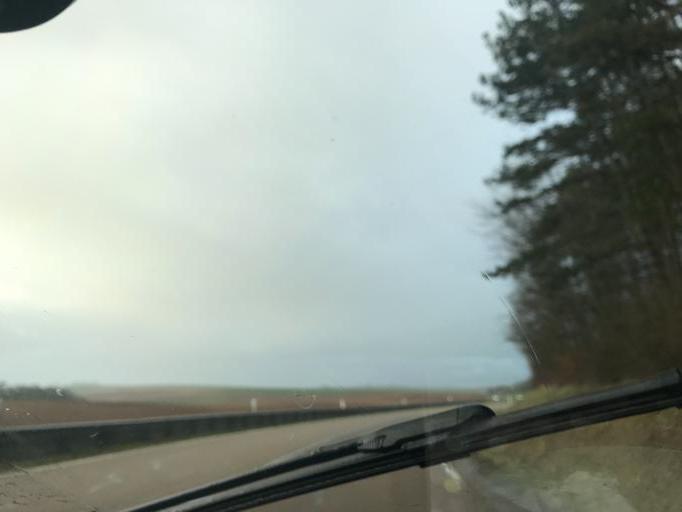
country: FR
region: Bourgogne
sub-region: Departement de l'Yonne
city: Fontenailles
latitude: 47.6322
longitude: 3.4906
